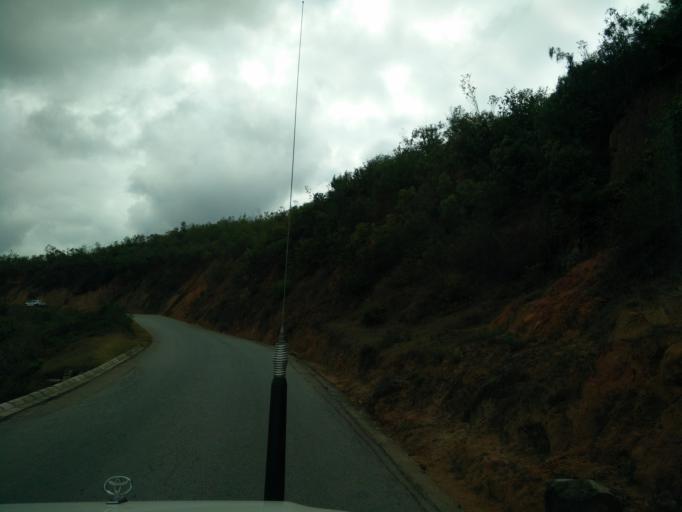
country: MG
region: Upper Matsiatra
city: Fandrandava
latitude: -21.2937
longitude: 47.2429
